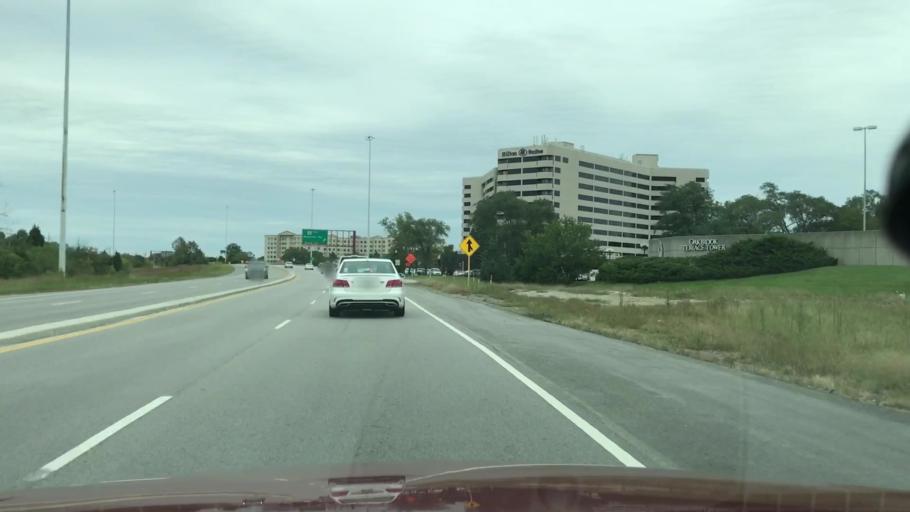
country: US
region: Illinois
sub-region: DuPage County
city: Oakbrook Terrace
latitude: 41.8583
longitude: -87.9564
